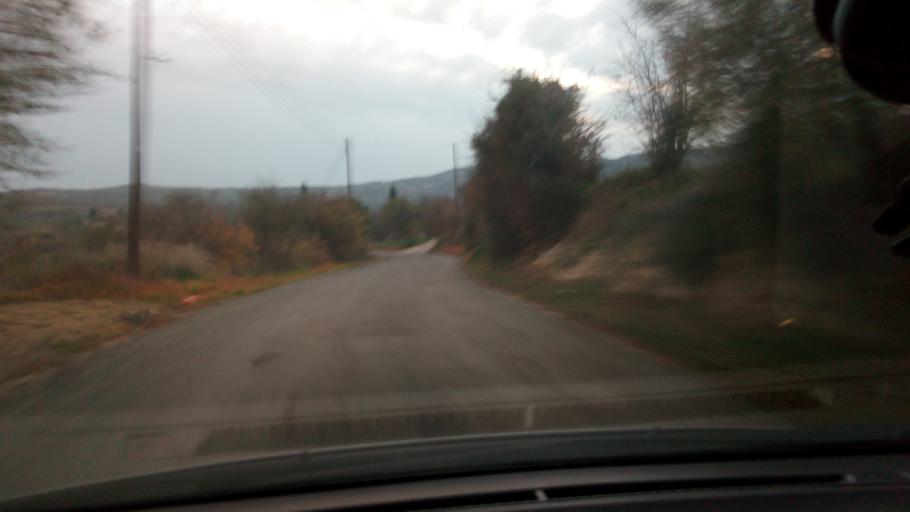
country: CY
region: Pafos
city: Tala
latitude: 34.9187
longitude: 32.4684
